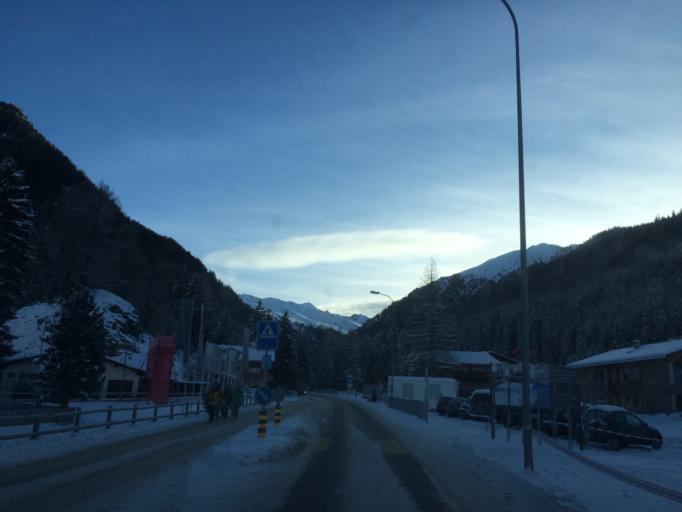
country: CH
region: Grisons
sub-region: Praettigau/Davos District
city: Davos
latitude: 46.8114
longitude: 9.8503
